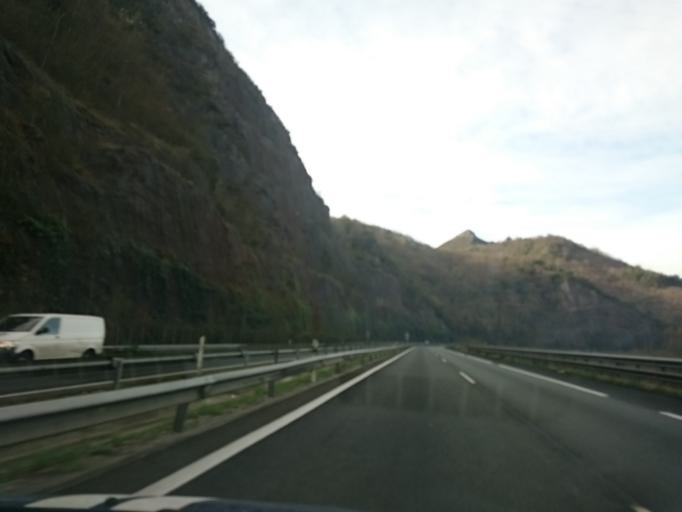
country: ES
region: Asturias
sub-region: Province of Asturias
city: Castandiello
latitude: 43.3019
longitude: -5.8505
